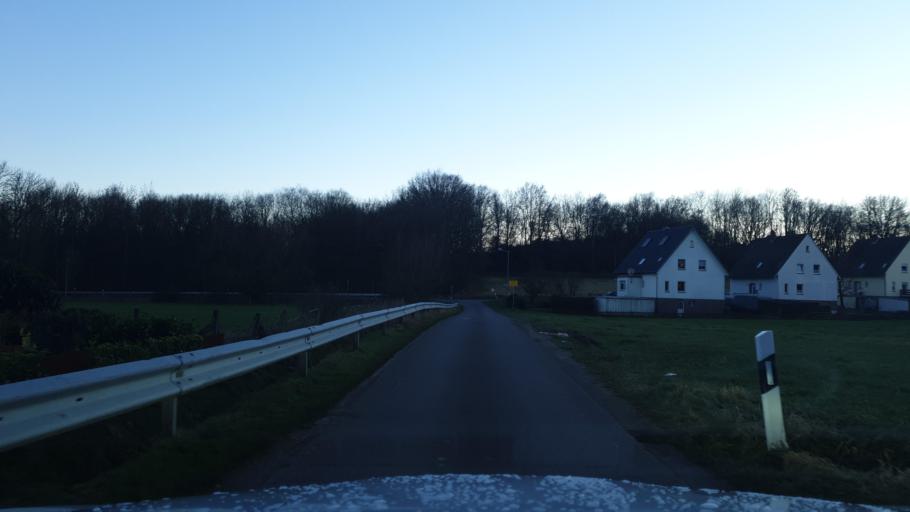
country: DE
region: North Rhine-Westphalia
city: Bad Oeynhausen
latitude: 52.2390
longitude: 8.8284
